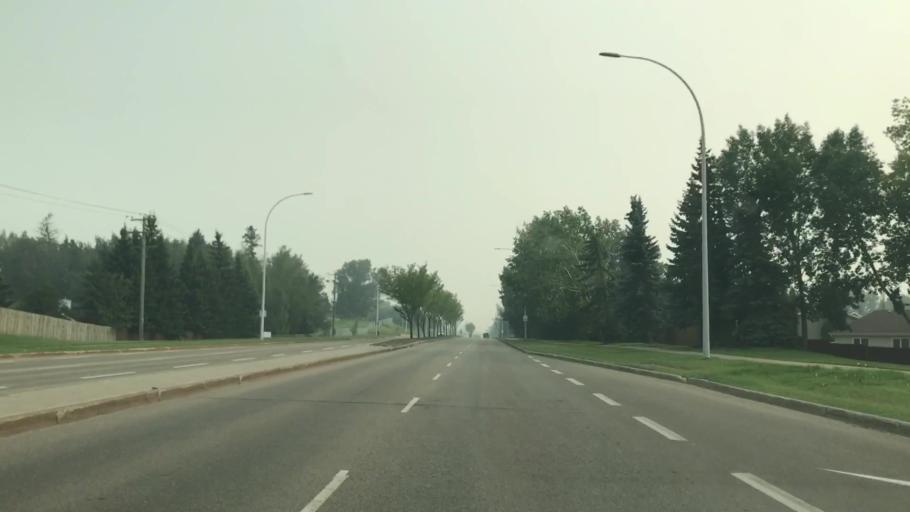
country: CA
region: Alberta
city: Sherwood Park
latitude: 53.5343
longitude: -113.3202
